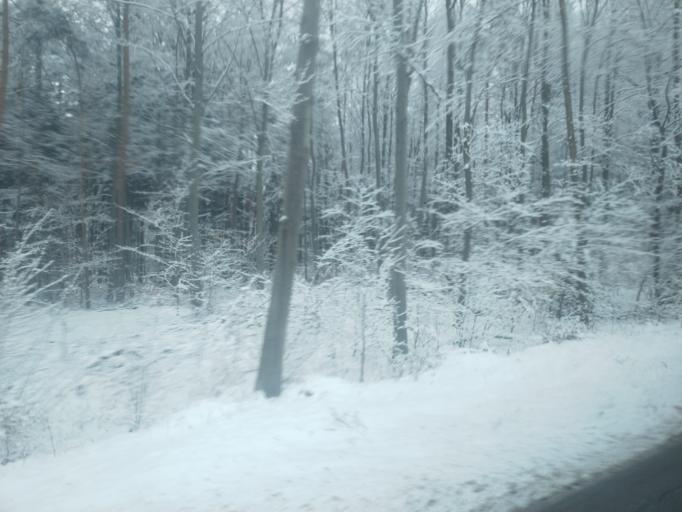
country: DE
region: Baden-Wuerttemberg
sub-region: Karlsruhe Region
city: Neuenburg
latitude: 48.8568
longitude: 8.5766
